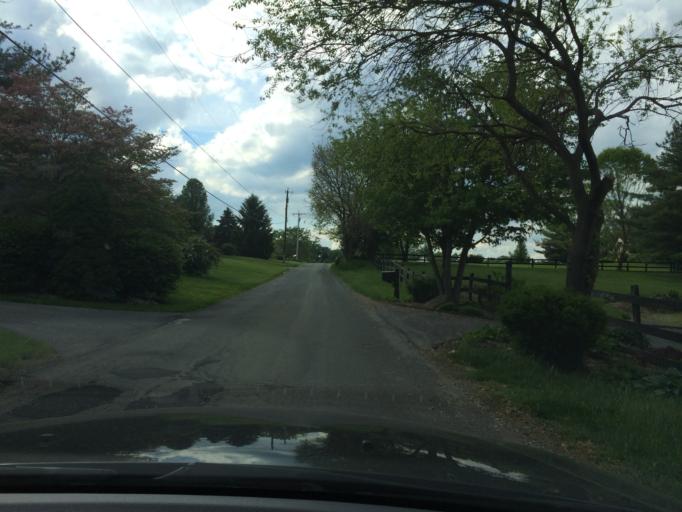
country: US
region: Maryland
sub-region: Carroll County
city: Westminster
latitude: 39.4770
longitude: -77.0267
